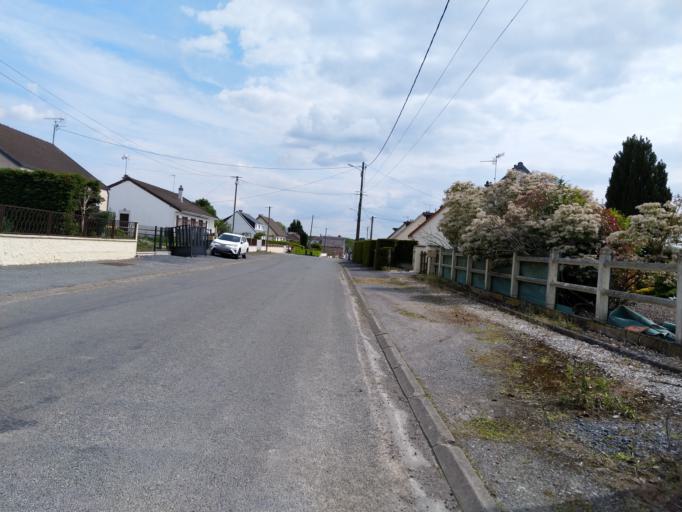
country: FR
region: Picardie
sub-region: Departement de l'Aisne
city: Boue
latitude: 50.0155
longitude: 3.6932
